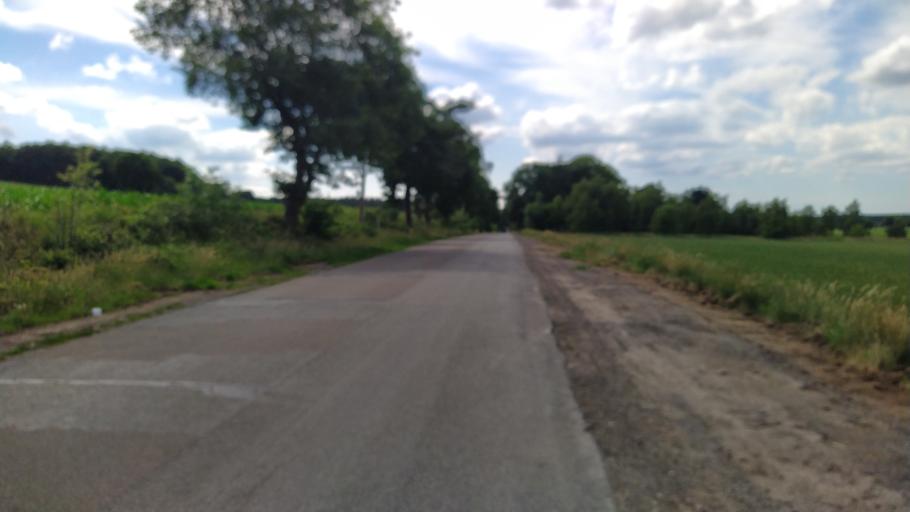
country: DE
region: Lower Saxony
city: Armstorf
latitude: 53.6060
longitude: 9.0571
